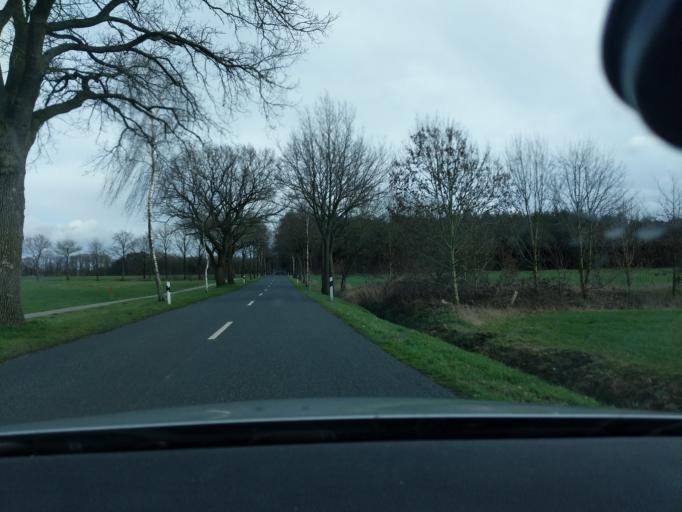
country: DE
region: Lower Saxony
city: Oldendorf
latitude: 53.5831
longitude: 9.2832
